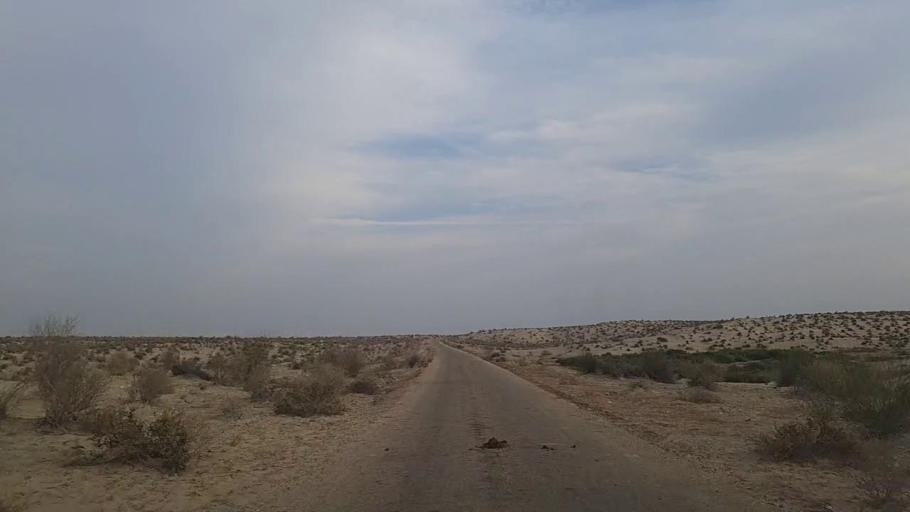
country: PK
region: Sindh
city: Daur
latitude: 26.5058
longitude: 68.5149
